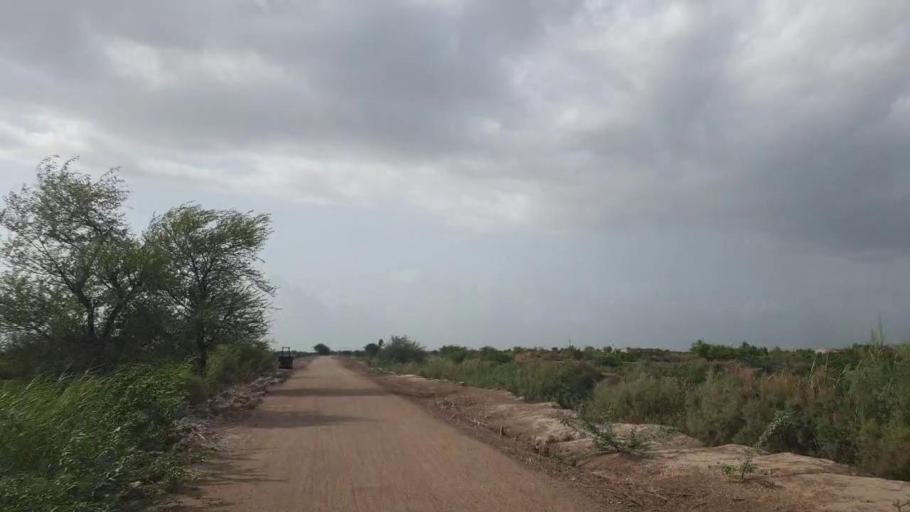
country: PK
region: Sindh
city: Kadhan
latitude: 24.5763
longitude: 69.0598
